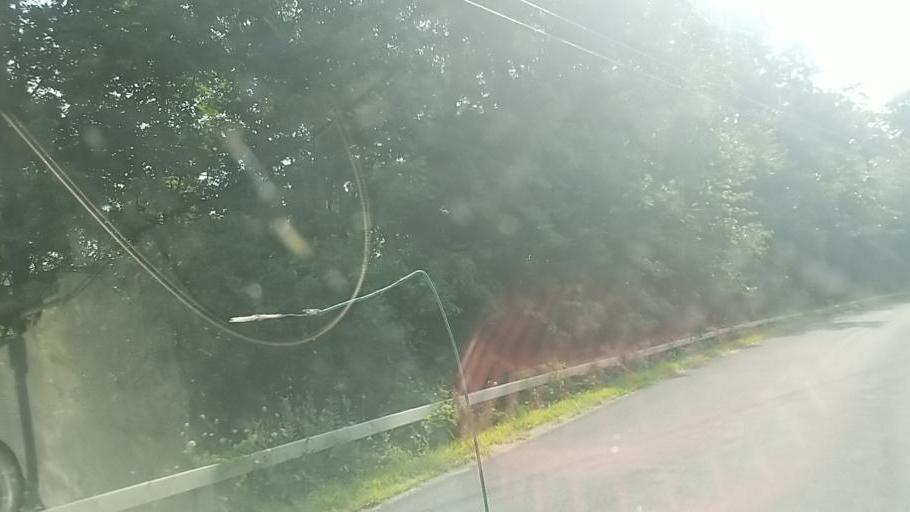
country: US
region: New York
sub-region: Montgomery County
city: Fonda
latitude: 42.9684
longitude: -74.4244
